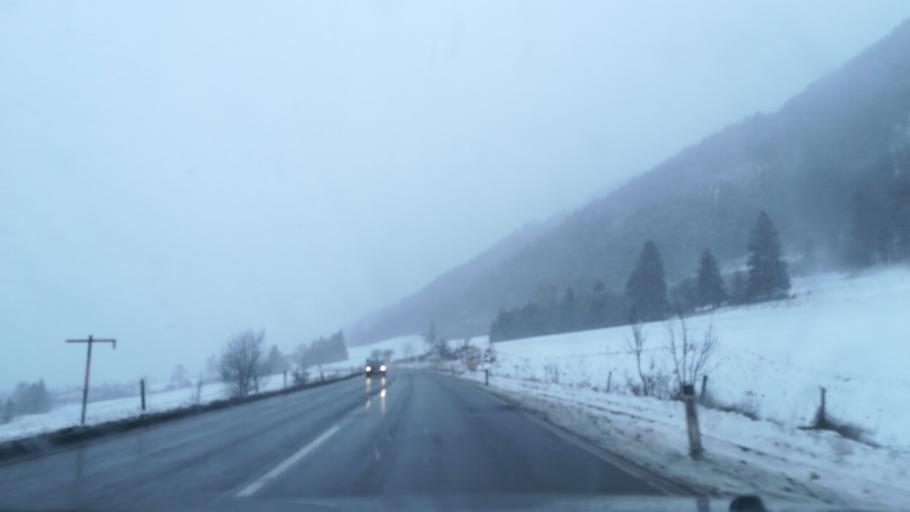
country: AT
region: Styria
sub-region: Politischer Bezirk Murtal
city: Sankt Peter ob Judenburg
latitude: 47.1942
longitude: 14.5980
